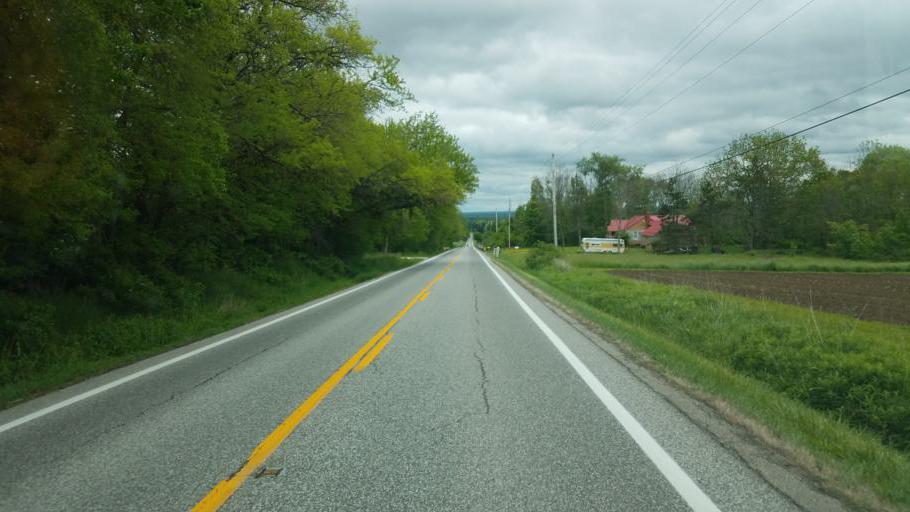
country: US
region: Ohio
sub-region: Geauga County
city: Middlefield
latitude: 41.3889
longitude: -81.0249
